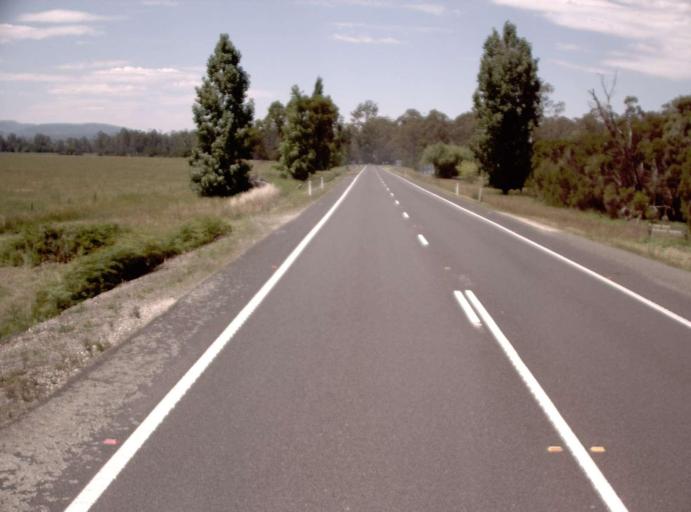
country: AU
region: New South Wales
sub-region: Bombala
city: Bombala
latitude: -37.5698
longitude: 149.1384
